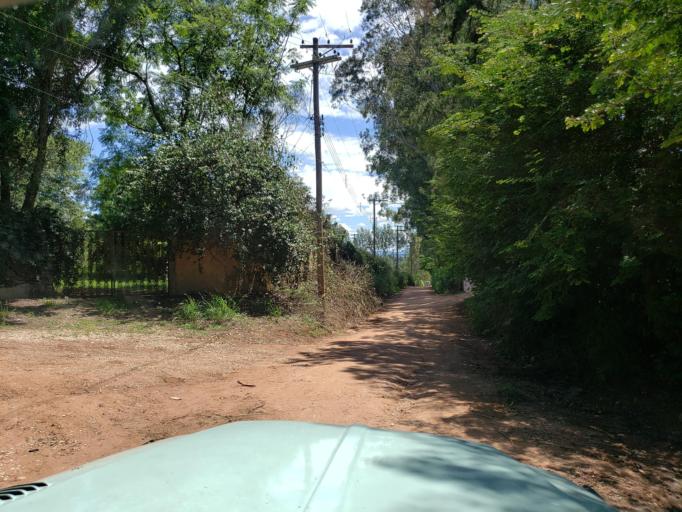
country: BR
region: Sao Paulo
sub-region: Moji-Guacu
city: Mogi-Gaucu
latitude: -22.3034
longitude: -46.9061
